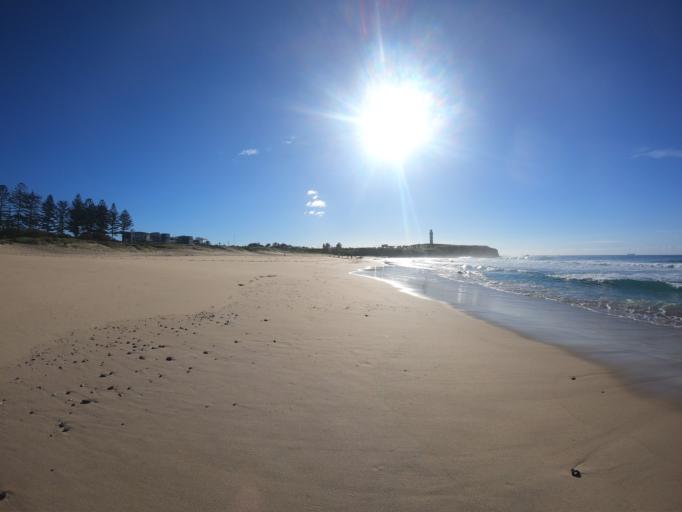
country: AU
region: New South Wales
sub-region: Wollongong
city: Wollongong
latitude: -34.4251
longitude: 150.9063
